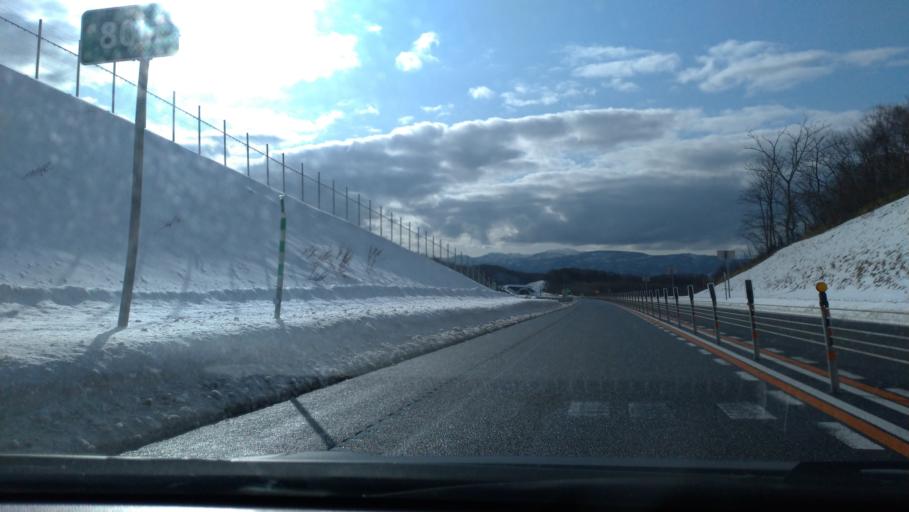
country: JP
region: Hokkaido
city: Yoichi
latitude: 43.1955
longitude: 140.8836
